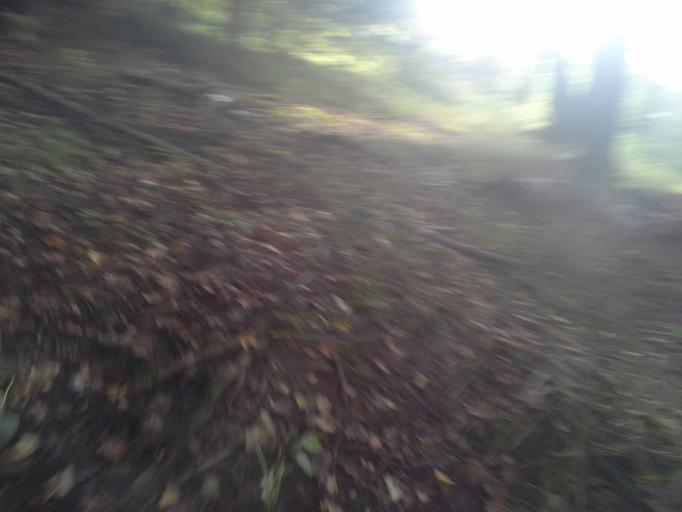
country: RU
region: Moskovskaya
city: Kievskij
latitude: 55.3476
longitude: 36.9574
